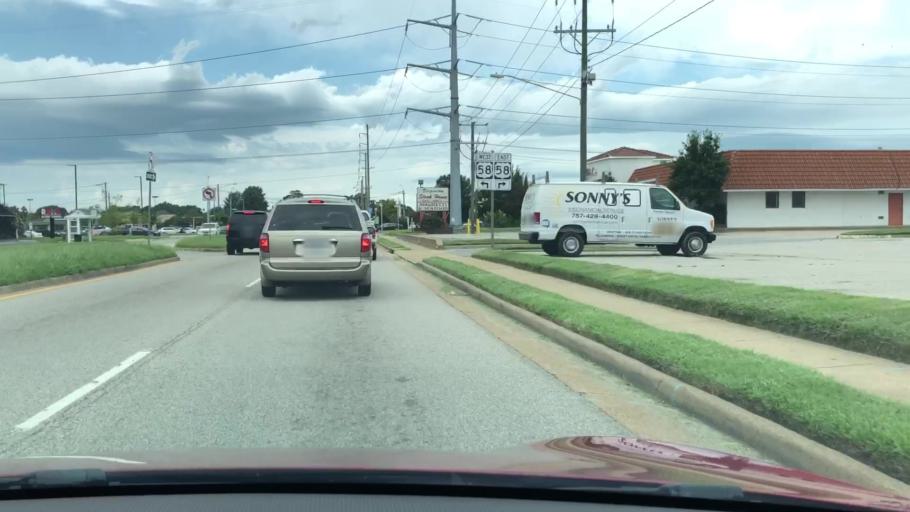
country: US
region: Virginia
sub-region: City of Virginia Beach
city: Virginia Beach
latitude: 36.8491
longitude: -76.0217
